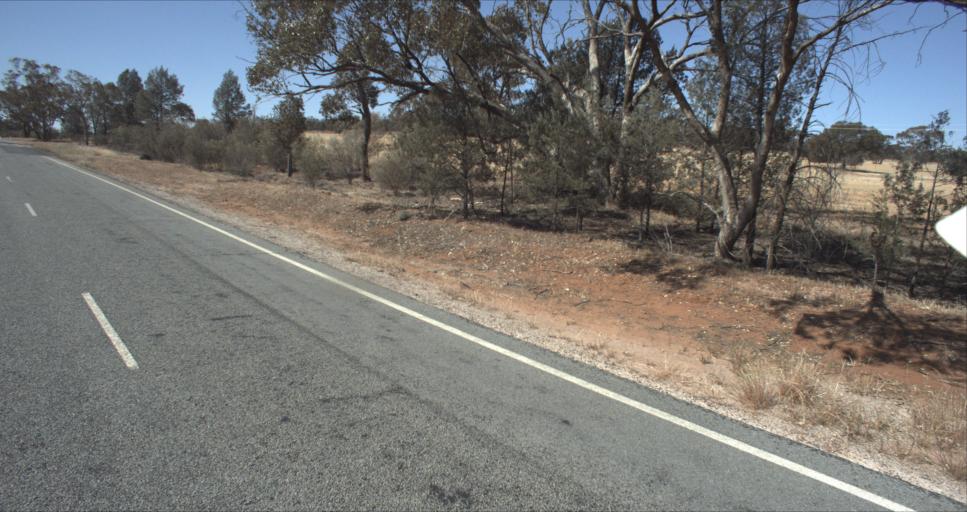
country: AU
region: New South Wales
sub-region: Leeton
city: Leeton
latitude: -34.4809
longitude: 146.4342
